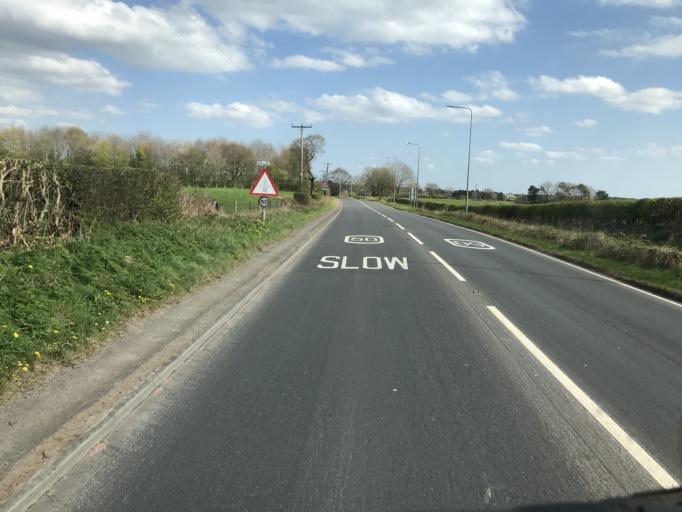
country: GB
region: England
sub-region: Cheshire West and Chester
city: Oakmere
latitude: 53.2111
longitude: -2.6753
